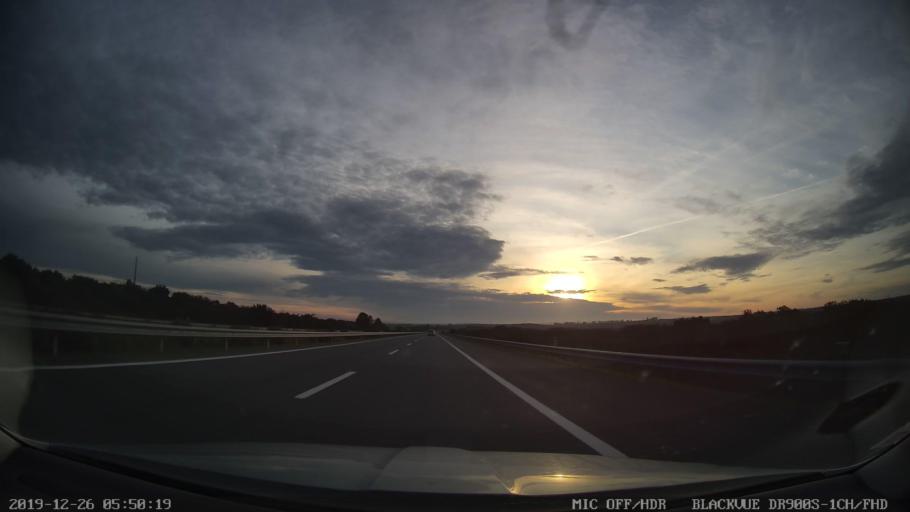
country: PT
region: Evora
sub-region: Evora
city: Evora
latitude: 38.6813
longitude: -7.8186
